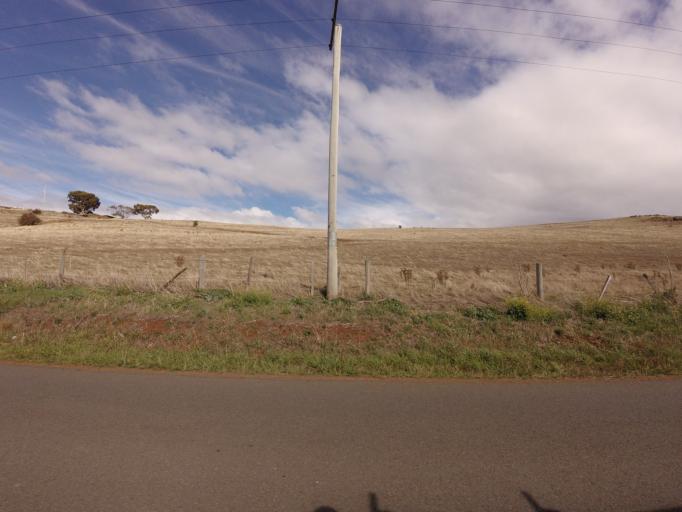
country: AU
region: Tasmania
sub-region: Derwent Valley
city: New Norfolk
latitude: -42.6979
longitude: 146.9278
